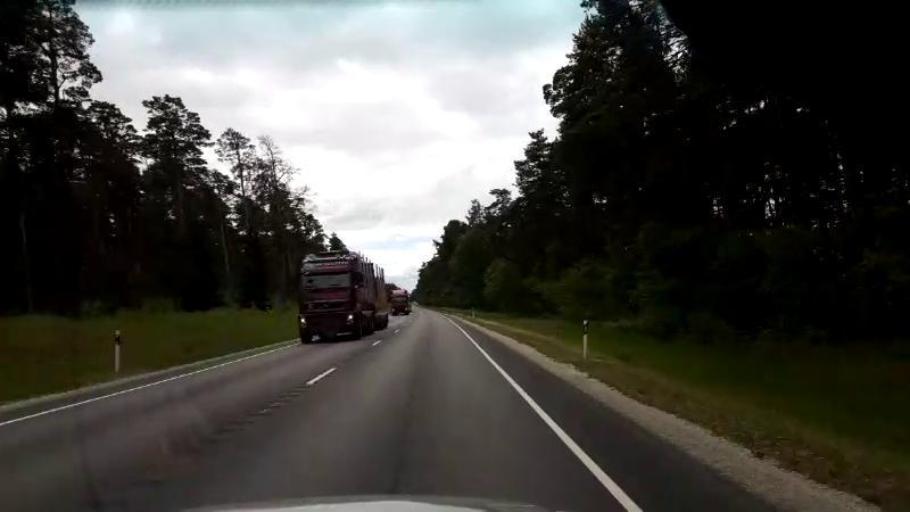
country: EE
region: Paernumaa
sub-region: Paernu linn
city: Parnu
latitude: 58.1720
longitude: 24.4950
